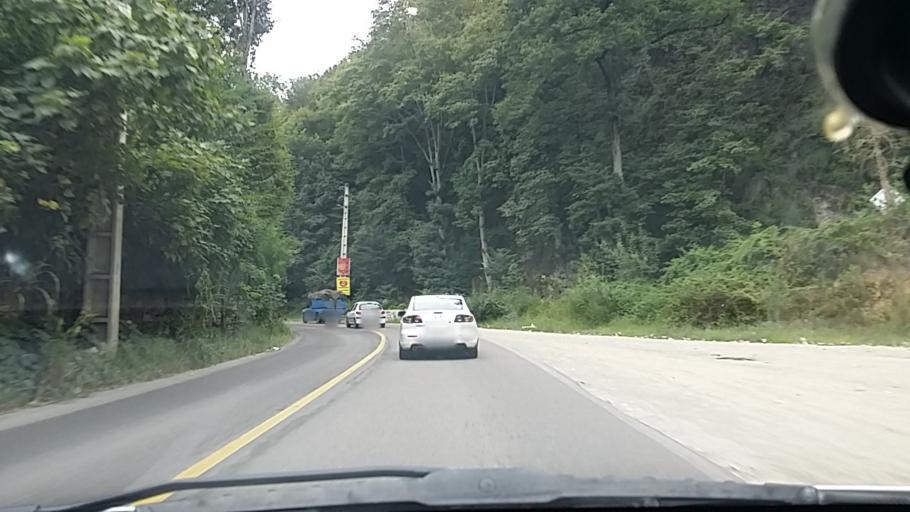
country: IR
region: Mazandaran
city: Chalus
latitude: 36.6093
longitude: 51.3871
